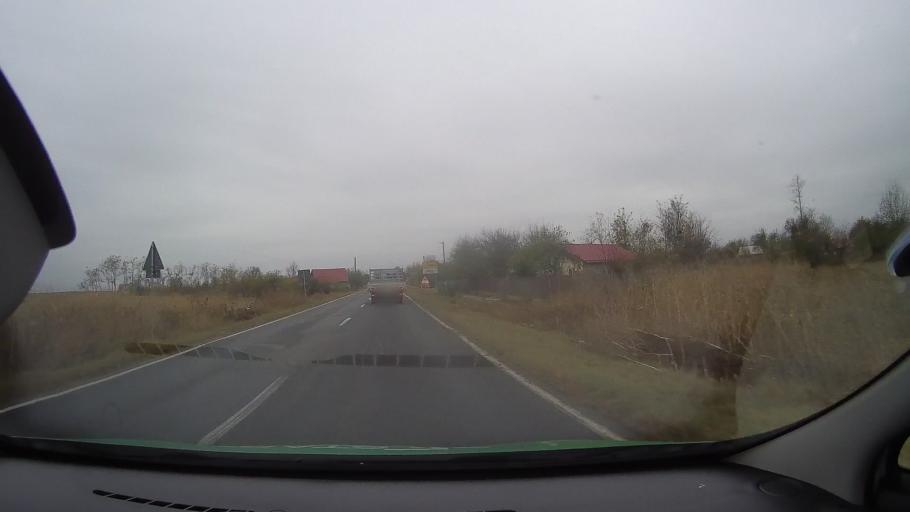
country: RO
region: Ialomita
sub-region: Comuna Scanteia
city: Iazu
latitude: 44.7310
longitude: 27.4281
